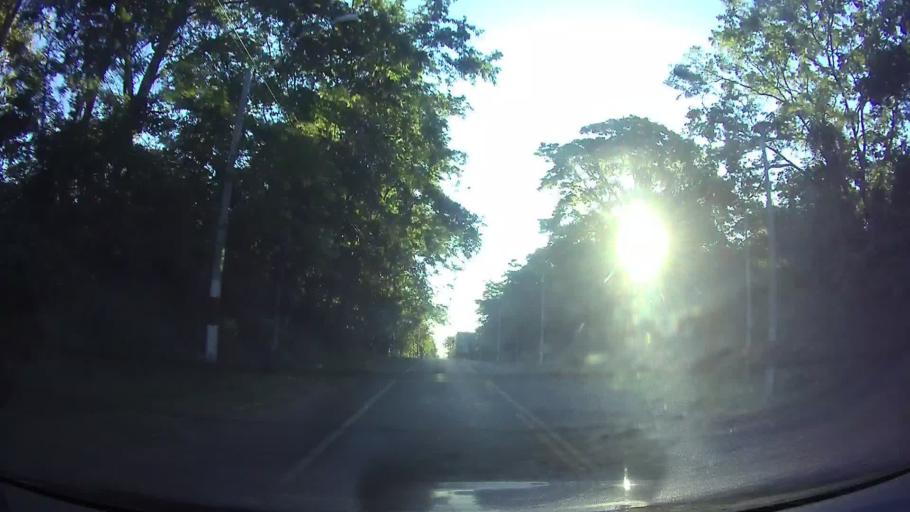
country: PY
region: Central
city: Aregua
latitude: -25.3263
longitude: -57.3960
